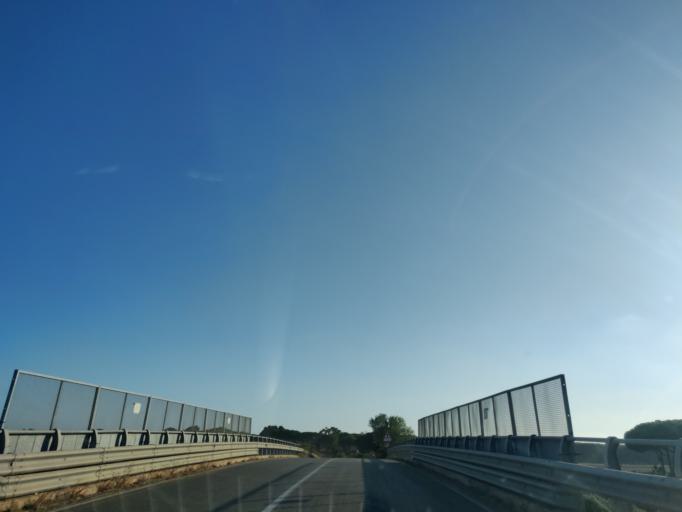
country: IT
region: Latium
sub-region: Provincia di Viterbo
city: Montalto di Castro
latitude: 42.2991
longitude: 11.6500
